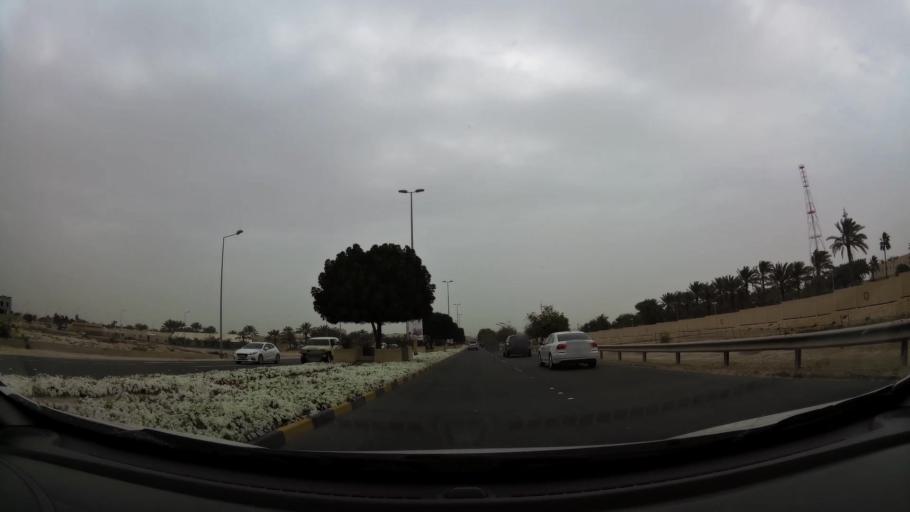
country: BH
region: Northern
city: Ar Rifa'
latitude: 26.1429
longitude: 50.5432
